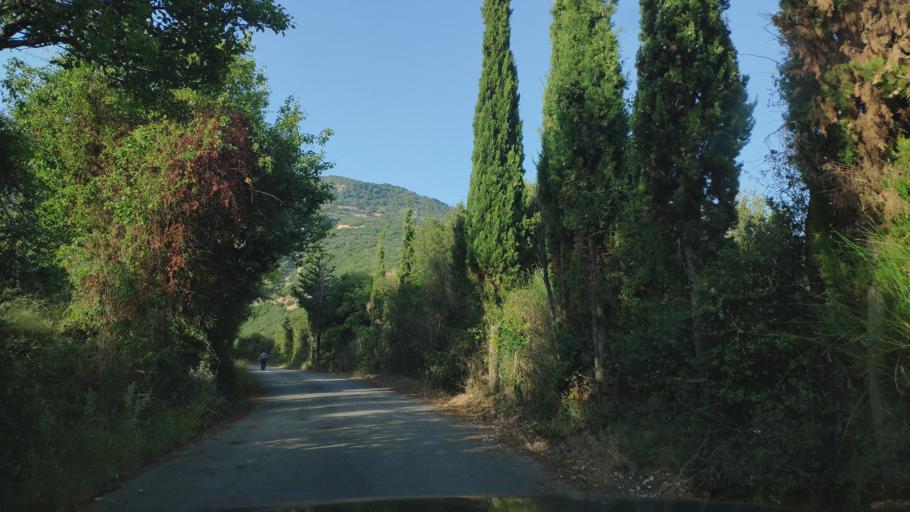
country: GR
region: West Greece
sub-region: Nomos Aitolias kai Akarnanias
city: Monastirakion
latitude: 38.8510
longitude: 20.9796
